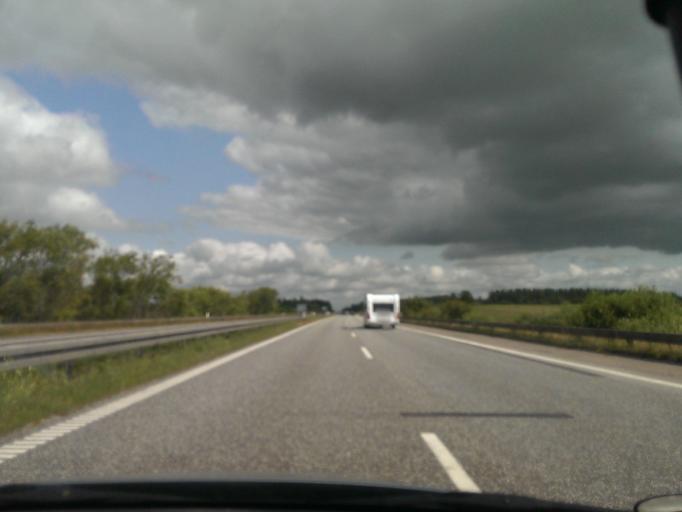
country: DK
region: North Denmark
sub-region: Mariagerfjord Kommune
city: Hobro
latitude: 56.6297
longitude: 9.7339
